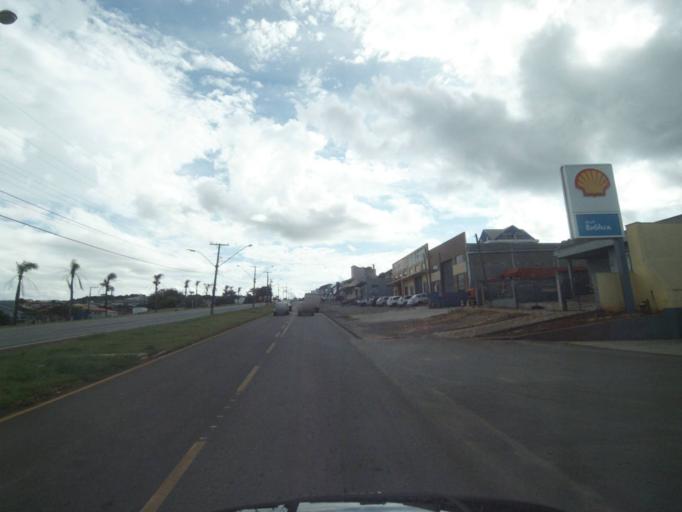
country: BR
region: Parana
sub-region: Telemaco Borba
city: Telemaco Borba
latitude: -24.3279
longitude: -50.6347
